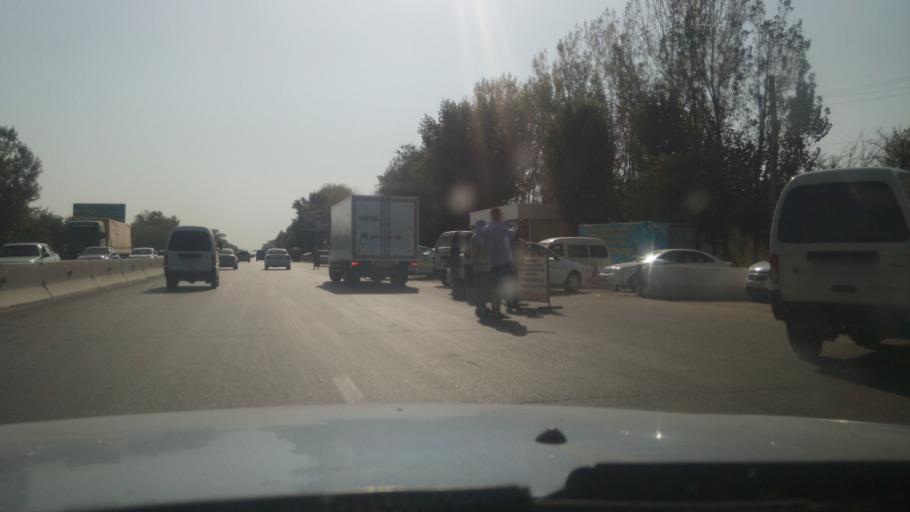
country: UZ
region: Toshkent
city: Urtaowul
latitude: 41.2284
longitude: 69.1483
